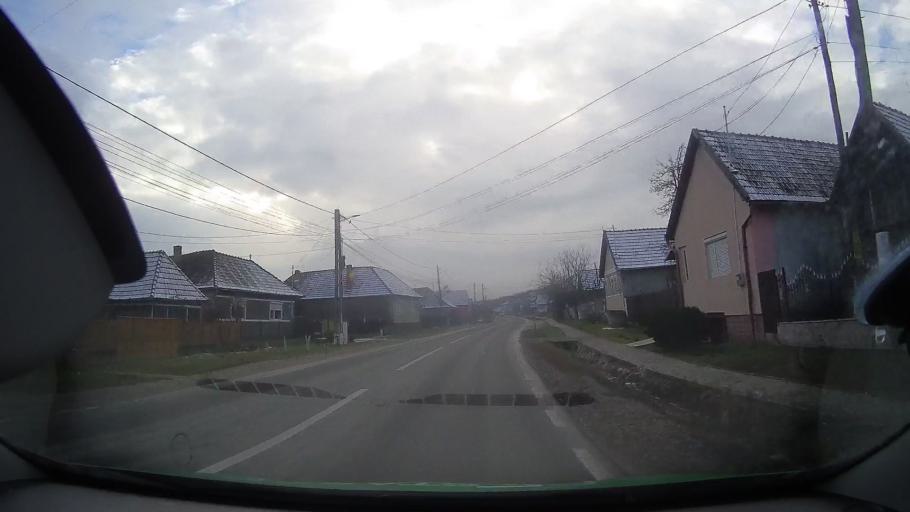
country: RO
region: Mures
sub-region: Comuna Cucerdea
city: Cucerdea
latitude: 46.4040
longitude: 24.2638
